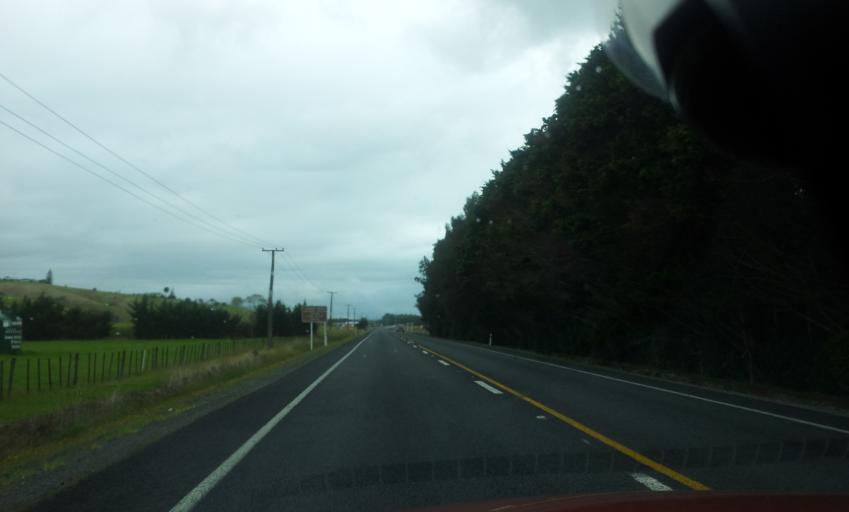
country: NZ
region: Northland
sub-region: Whangarei
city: Ruakaka
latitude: -35.8973
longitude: 174.4401
